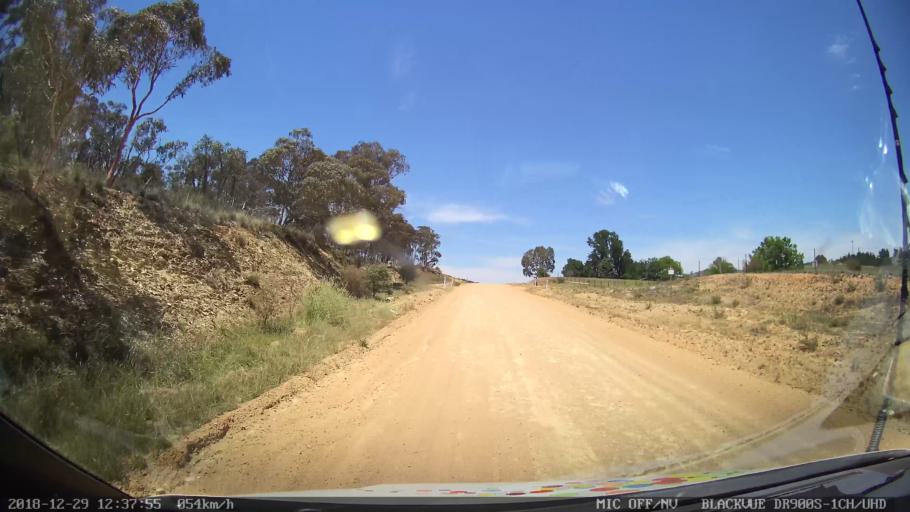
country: AU
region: Australian Capital Territory
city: Macarthur
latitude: -35.5845
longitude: 149.2291
